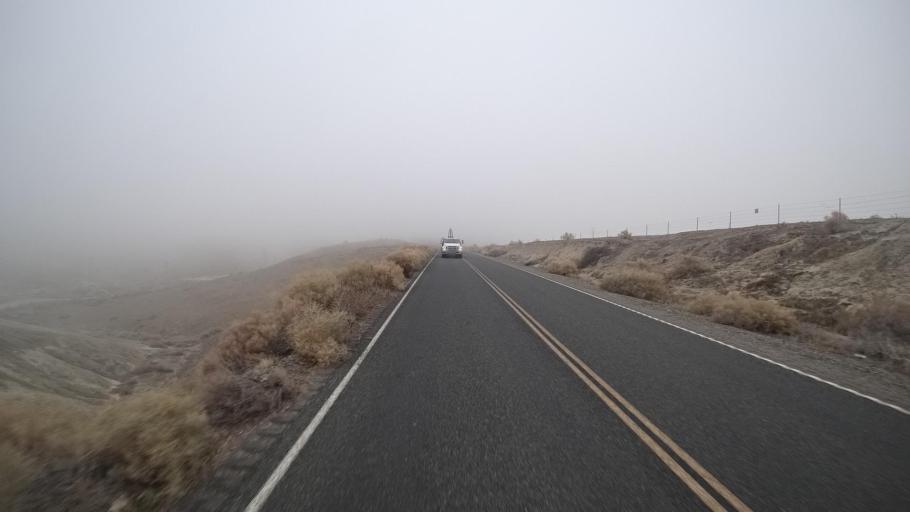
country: US
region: California
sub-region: Kern County
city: Buttonwillow
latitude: 35.2981
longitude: -119.4655
